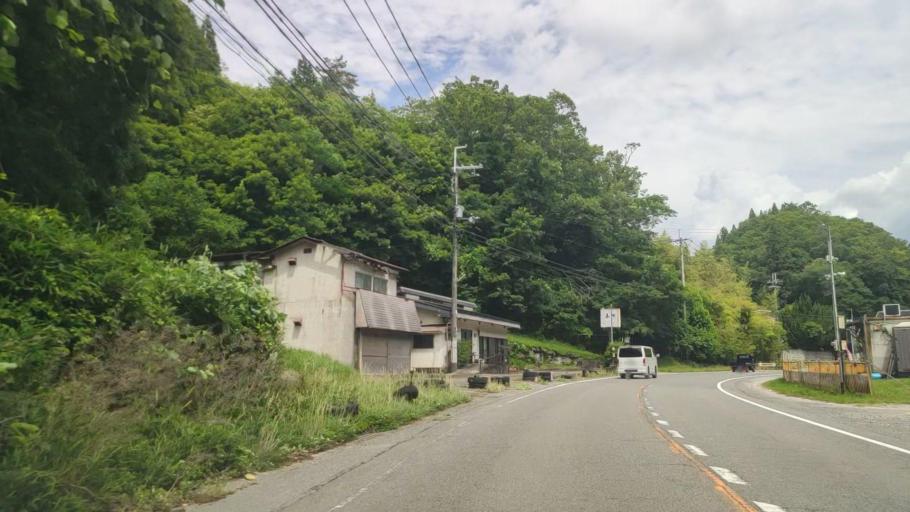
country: JP
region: Hyogo
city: Yamazakicho-nakabirose
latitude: 34.9923
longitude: 134.4017
